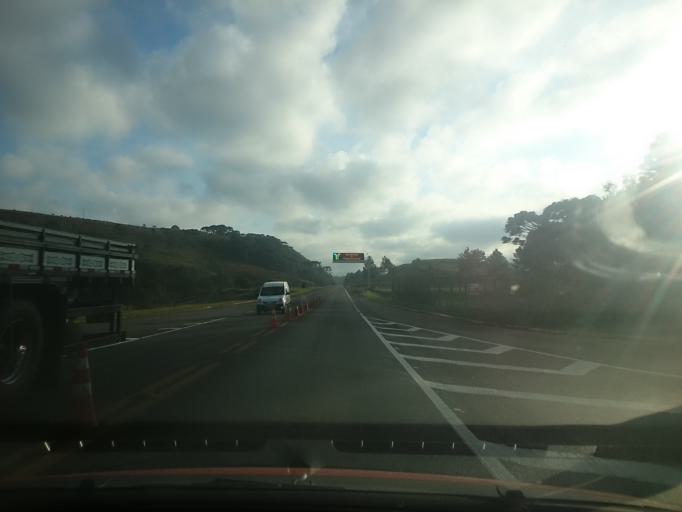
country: BR
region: Santa Catarina
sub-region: Lages
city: Lages
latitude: -28.0311
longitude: -50.5623
